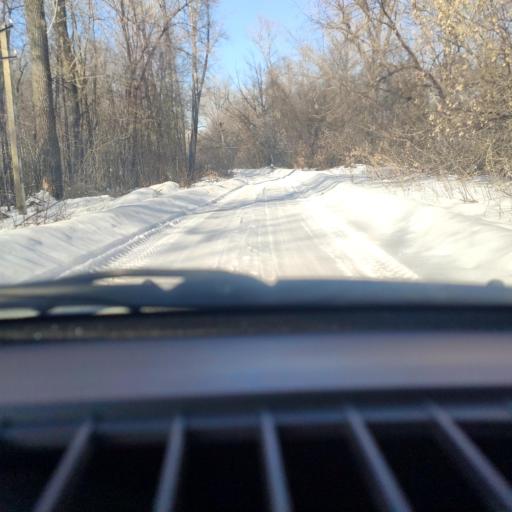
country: RU
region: Bashkortostan
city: Ufa
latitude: 54.6734
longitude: 55.9531
